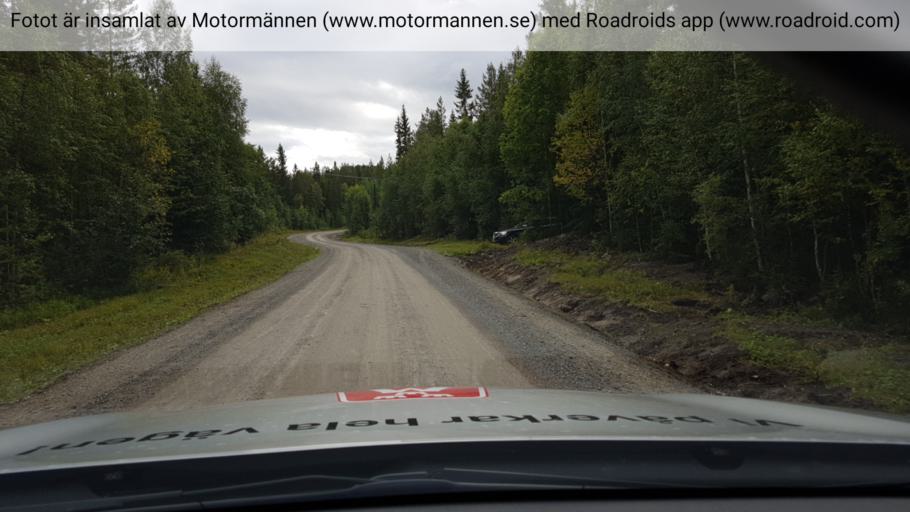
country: SE
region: Jaemtland
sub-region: Ragunda Kommun
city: Hammarstrand
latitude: 62.9249
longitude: 16.1232
